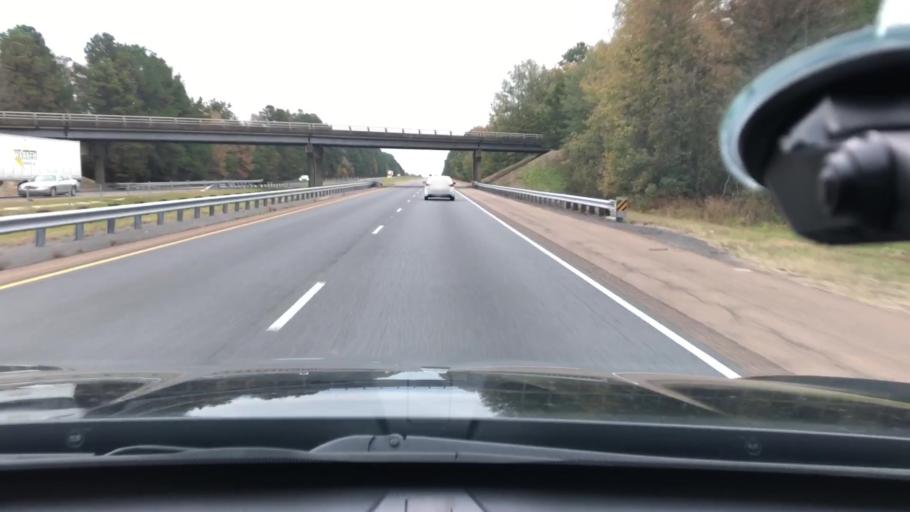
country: US
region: Arkansas
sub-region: Clark County
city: Gurdon
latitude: 33.9711
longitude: -93.2091
